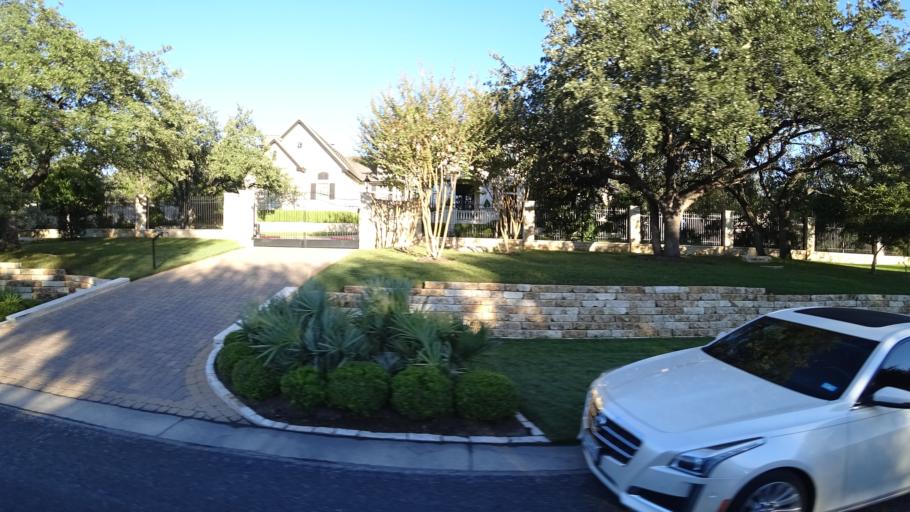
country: US
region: Texas
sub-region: Travis County
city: West Lake Hills
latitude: 30.3355
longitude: -97.8139
